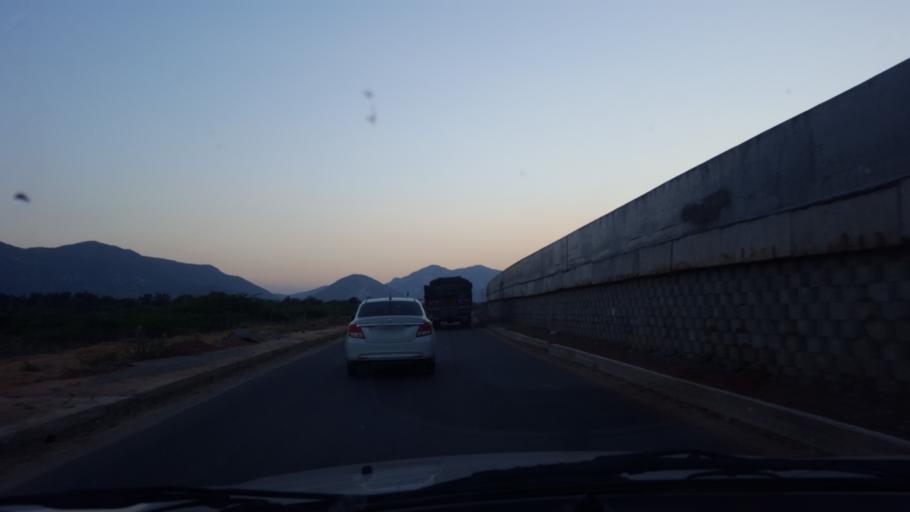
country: IN
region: Andhra Pradesh
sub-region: Chittoor
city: Narasingapuram
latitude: 13.5894
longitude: 79.3445
